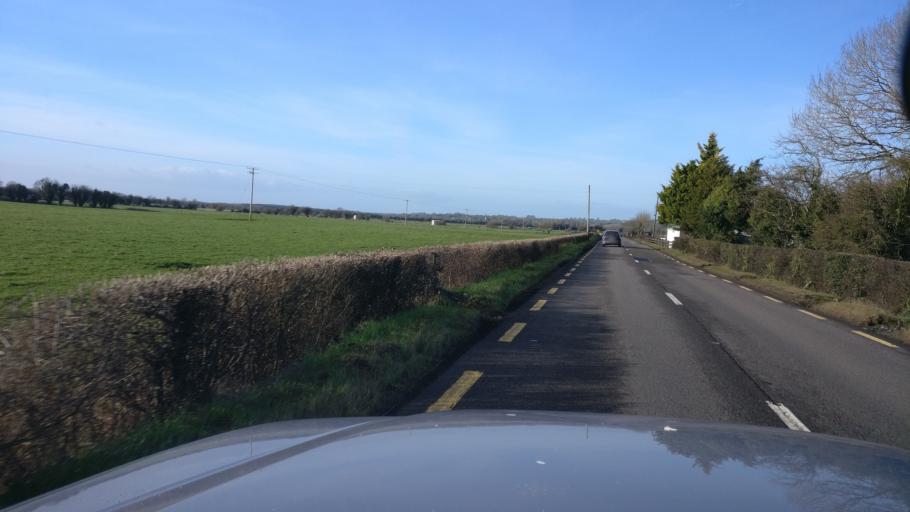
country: IE
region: Leinster
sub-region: Laois
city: Mountmellick
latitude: 53.1768
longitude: -7.3889
